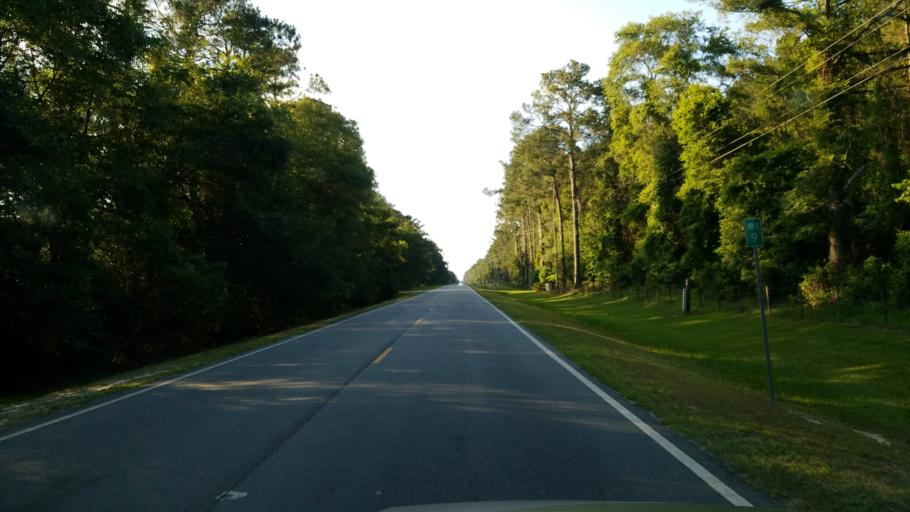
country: US
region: Georgia
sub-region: Lanier County
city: Lakeland
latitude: 31.0731
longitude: -83.0736
